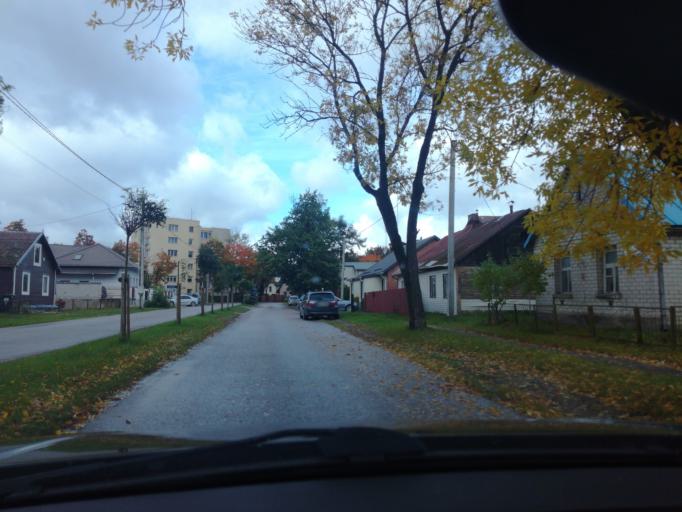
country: LT
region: Alytaus apskritis
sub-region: Alytus
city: Alytus
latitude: 54.3903
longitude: 24.0456
